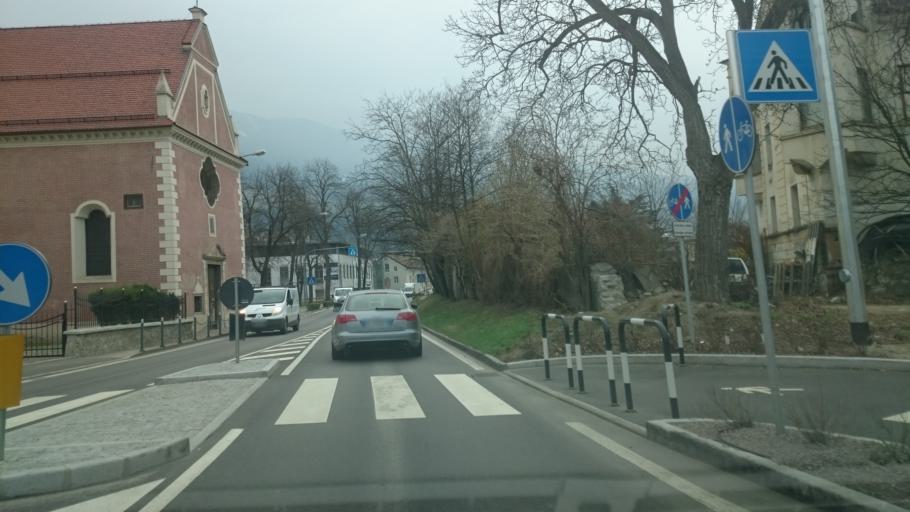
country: IT
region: Trentino-Alto Adige
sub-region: Bolzano
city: Leone-Santa Elisabetta
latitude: 46.7255
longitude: 11.6539
